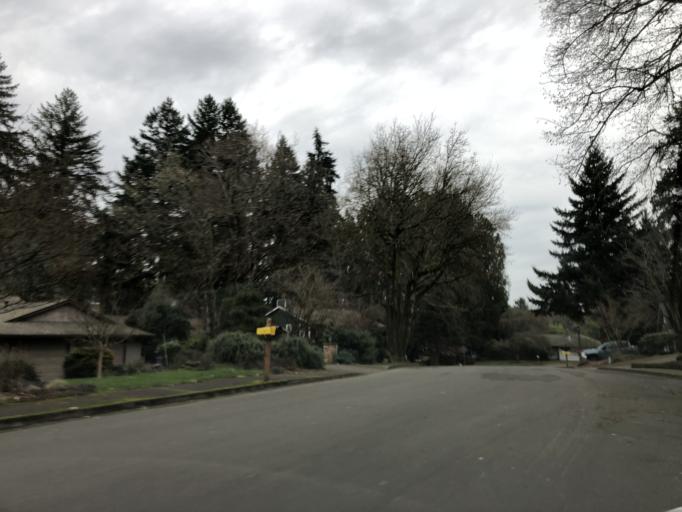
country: US
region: Oregon
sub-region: Washington County
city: Tigard
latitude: 45.4281
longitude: -122.7910
